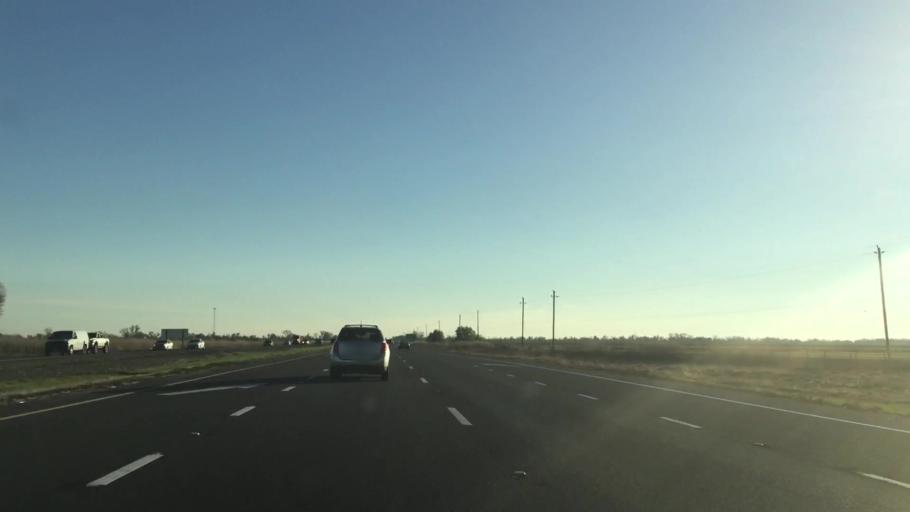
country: US
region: California
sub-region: Sacramento County
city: Elverta
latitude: 38.8362
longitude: -121.5439
